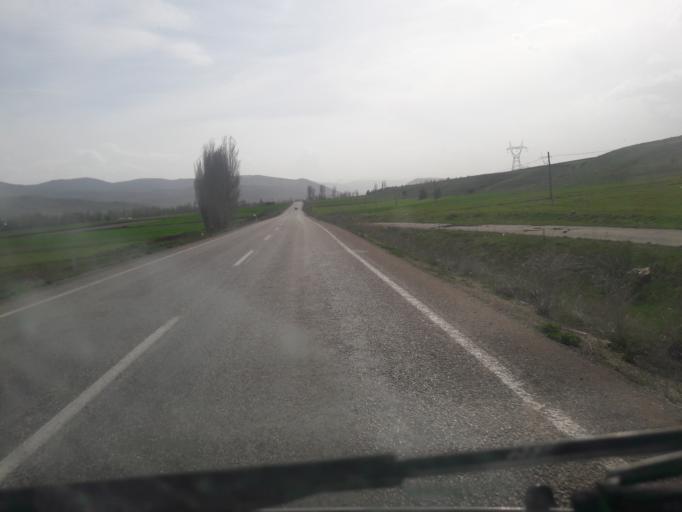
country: TR
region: Gumushane
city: Kelkit
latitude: 40.1364
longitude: 39.3818
